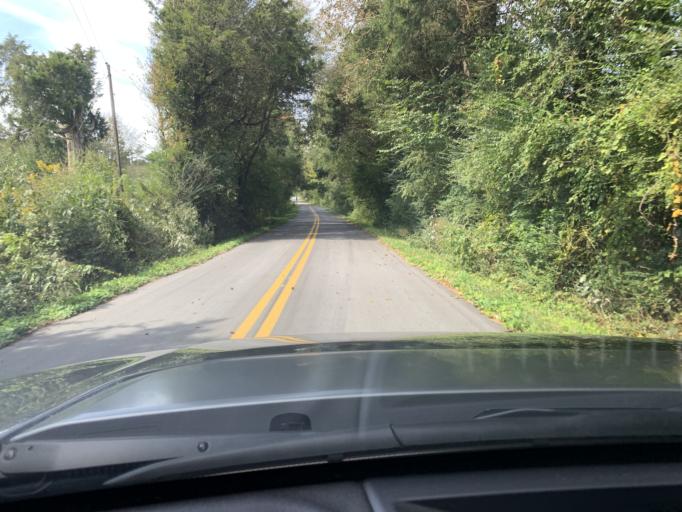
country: US
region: Georgia
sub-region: Floyd County
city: Cave Spring
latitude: 33.9491
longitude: -85.3834
